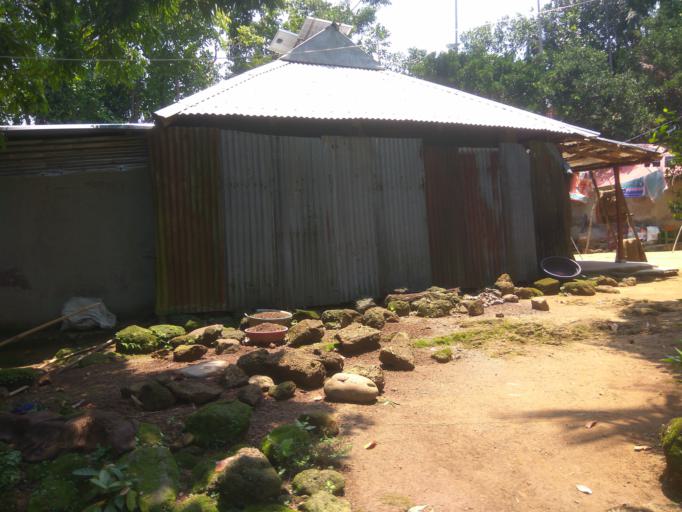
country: IN
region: Assam
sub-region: Karimganj
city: Karimganj
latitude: 25.0263
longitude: 92.4209
